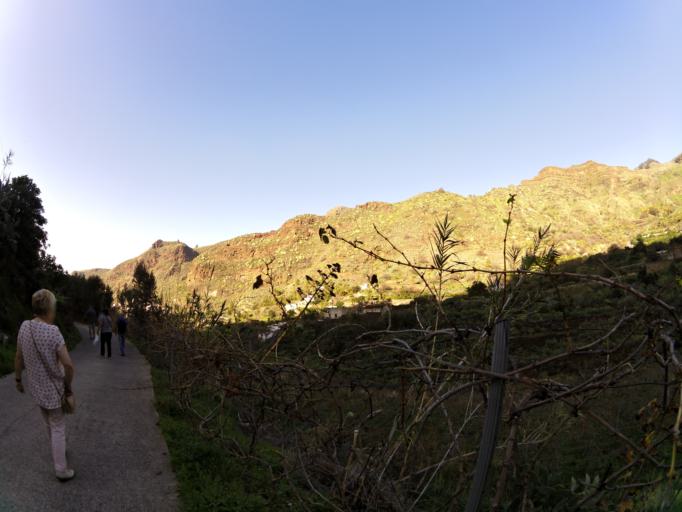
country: ES
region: Canary Islands
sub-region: Provincia de Las Palmas
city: Agaete
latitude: 28.0763
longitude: -15.6698
